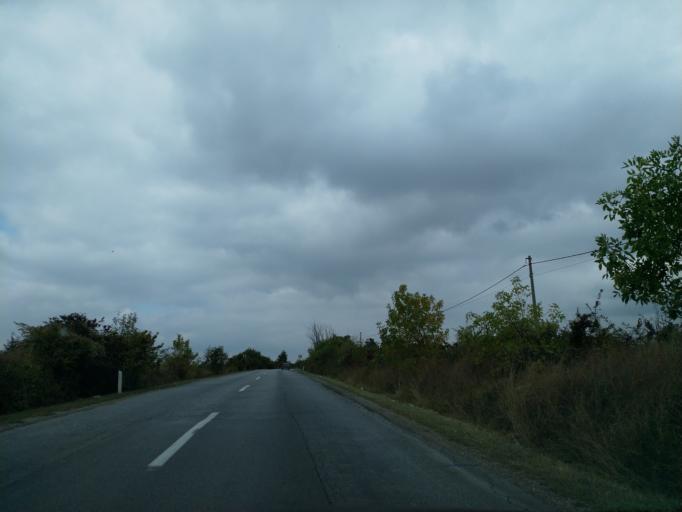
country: RS
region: Central Serbia
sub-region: Sumadijski Okrug
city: Topola
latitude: 44.1383
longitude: 20.7457
